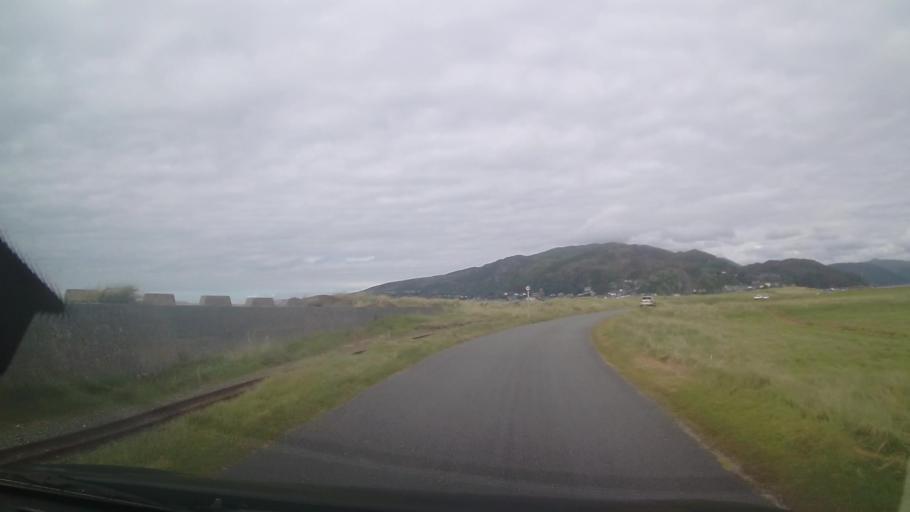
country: GB
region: Wales
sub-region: Gwynedd
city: Barmouth
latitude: 52.7075
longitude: -4.0589
